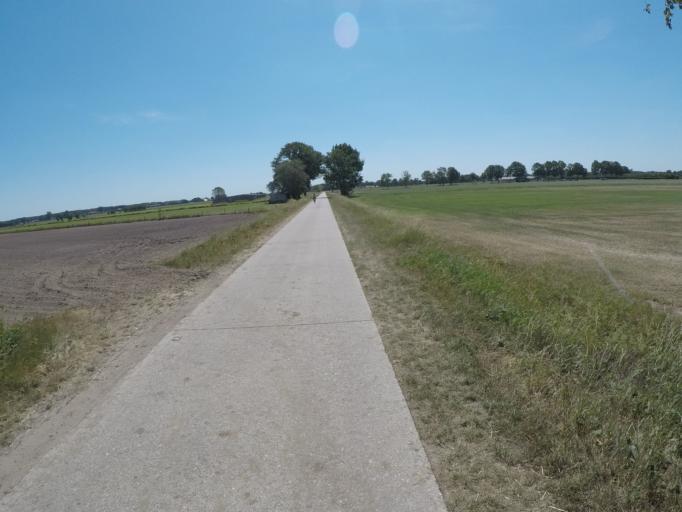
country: BE
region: Flanders
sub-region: Provincie Antwerpen
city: Brecht
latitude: 51.3785
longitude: 4.6959
